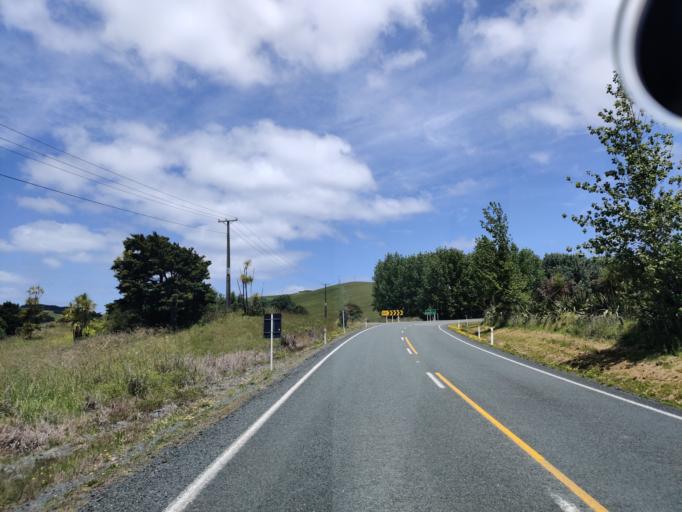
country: NZ
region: Auckland
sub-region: Auckland
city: Wellsford
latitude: -36.3794
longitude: 174.4510
